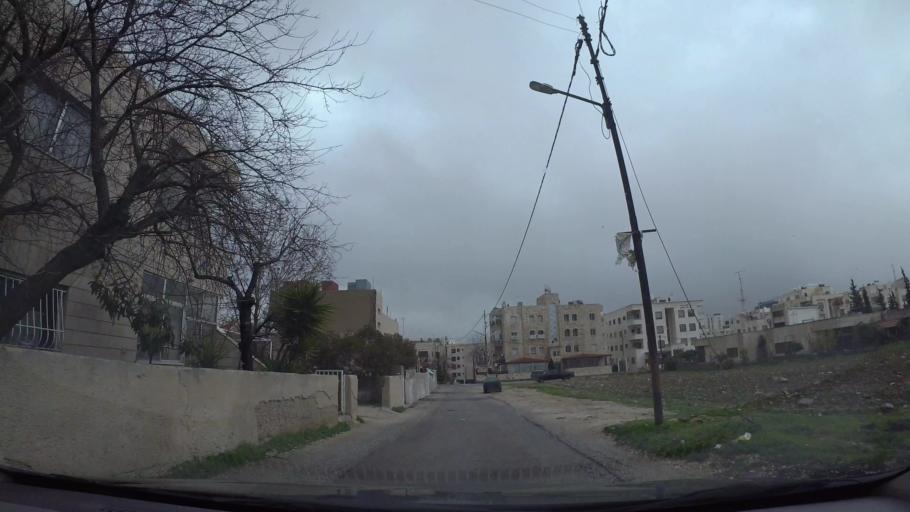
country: JO
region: Amman
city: Wadi as Sir
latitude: 31.9573
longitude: 35.8512
